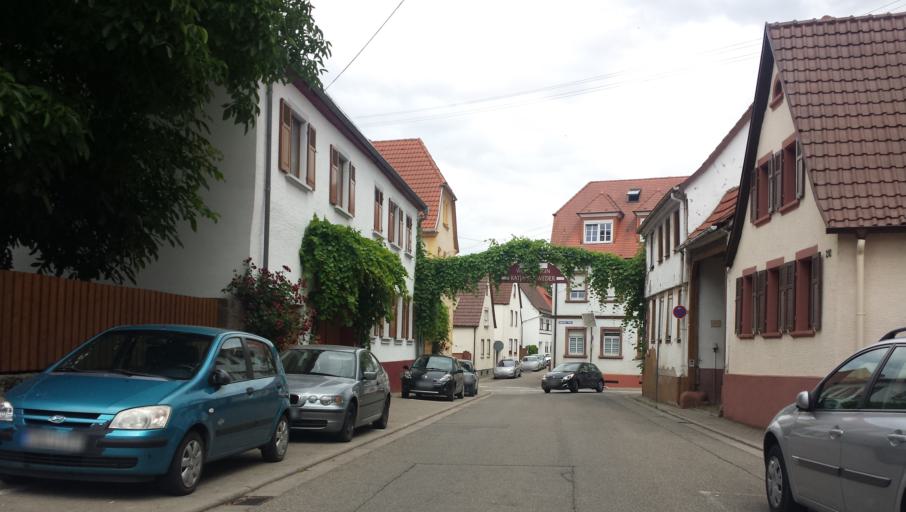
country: DE
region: Rheinland-Pfalz
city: Hochstadt
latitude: 49.2419
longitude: 8.2202
